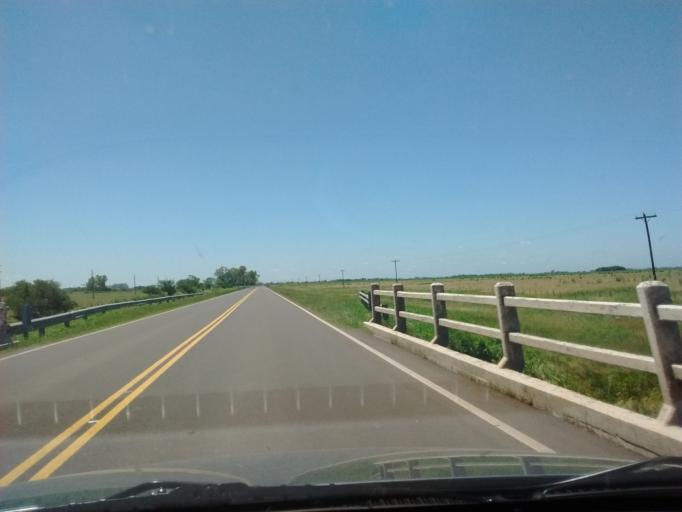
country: AR
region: Entre Rios
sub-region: Departamento de Gualeguay
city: Gualeguay
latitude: -33.0151
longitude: -59.4763
